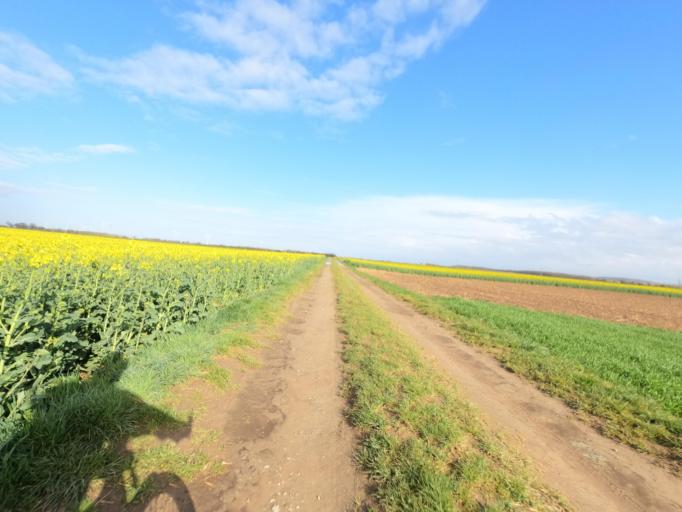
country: DE
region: North Rhine-Westphalia
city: Huckelhoven
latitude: 51.0052
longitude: 6.2053
